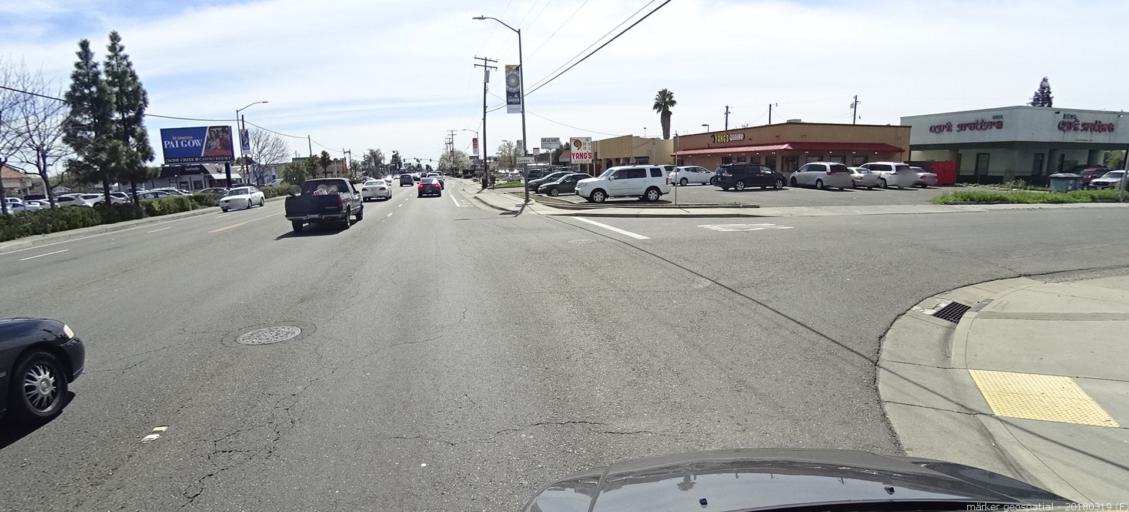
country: US
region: California
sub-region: Sacramento County
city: Parkway
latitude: 38.5208
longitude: -121.4407
